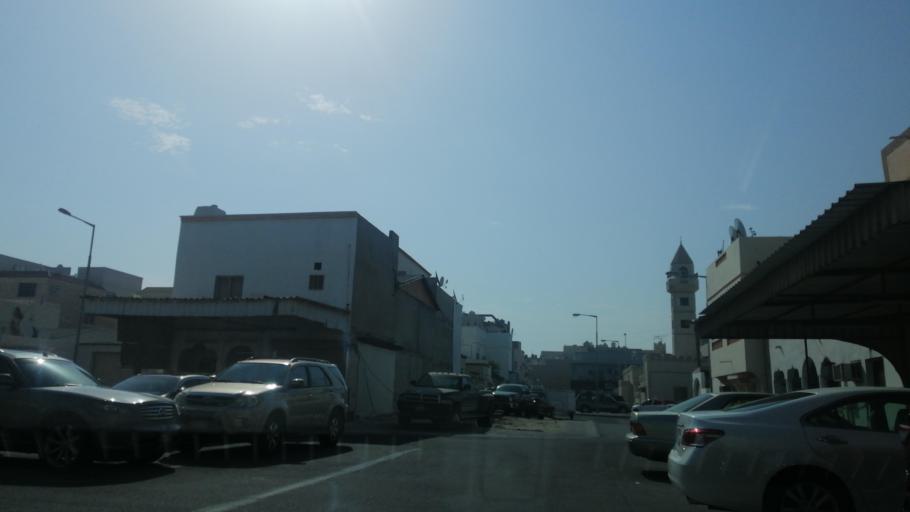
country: BH
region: Muharraq
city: Al Muharraq
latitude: 26.2562
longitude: 50.6307
